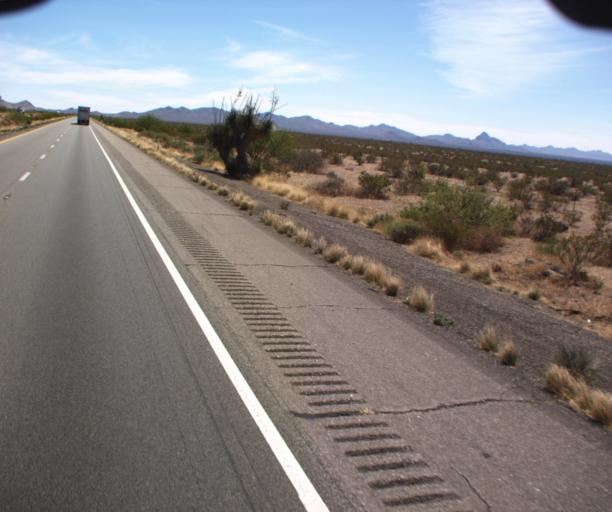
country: US
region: New Mexico
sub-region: Hidalgo County
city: Lordsburg
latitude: 32.2442
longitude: -109.1222
